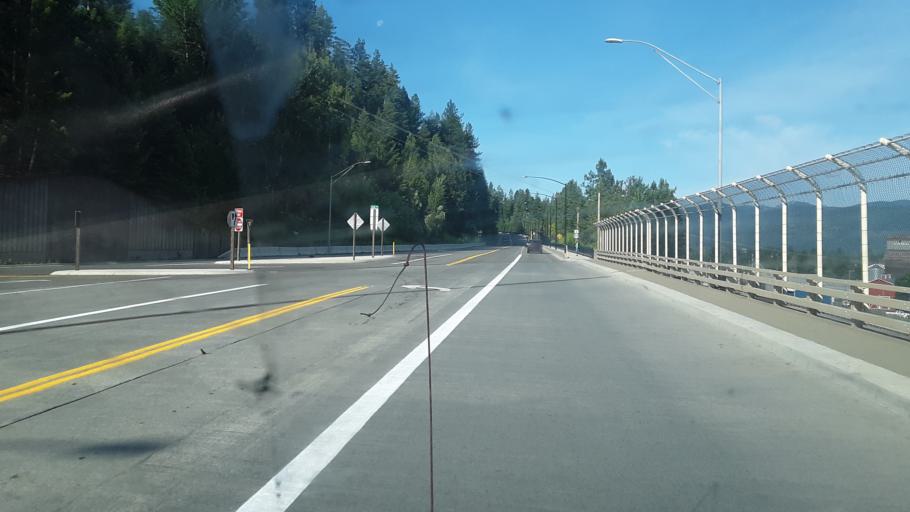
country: US
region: Idaho
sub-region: Boundary County
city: Bonners Ferry
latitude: 48.6956
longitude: -116.3106
